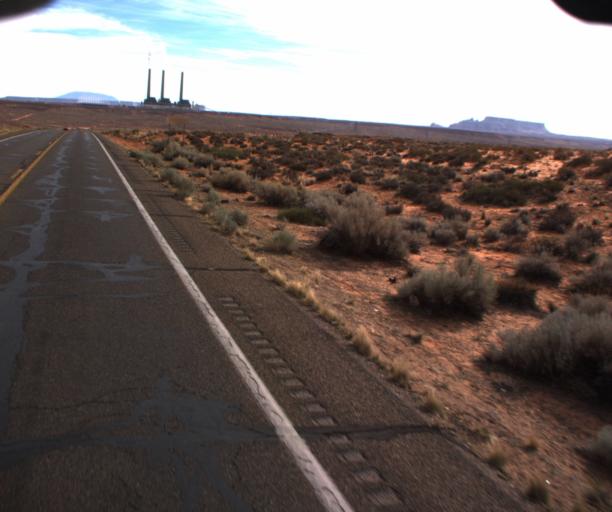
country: US
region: Arizona
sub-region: Coconino County
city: LeChee
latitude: 36.8982
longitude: -111.4295
